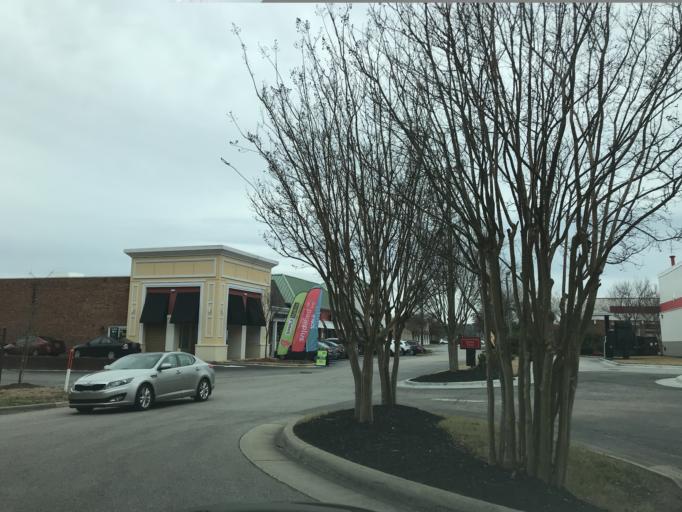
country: US
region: North Carolina
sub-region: Wake County
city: Raleigh
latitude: 35.8719
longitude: -78.5789
